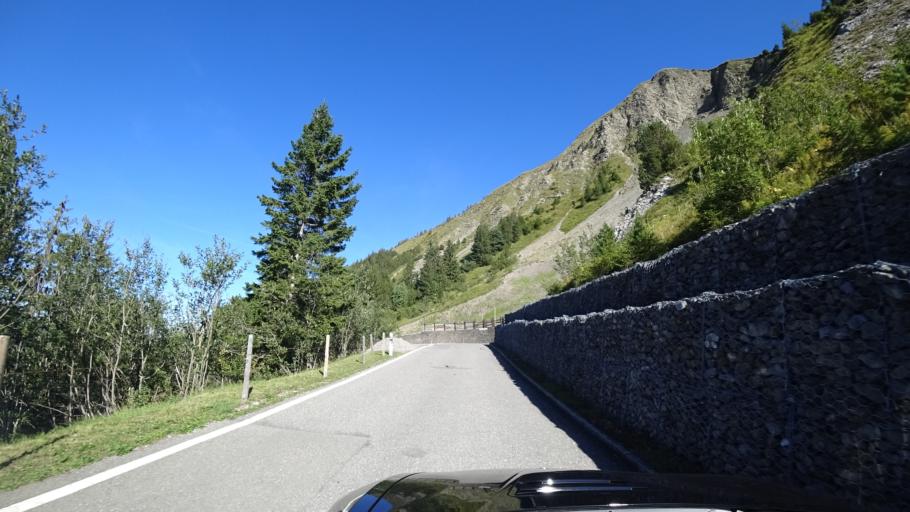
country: CH
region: Obwalden
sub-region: Obwalden
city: Lungern
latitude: 46.8187
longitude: 8.0923
